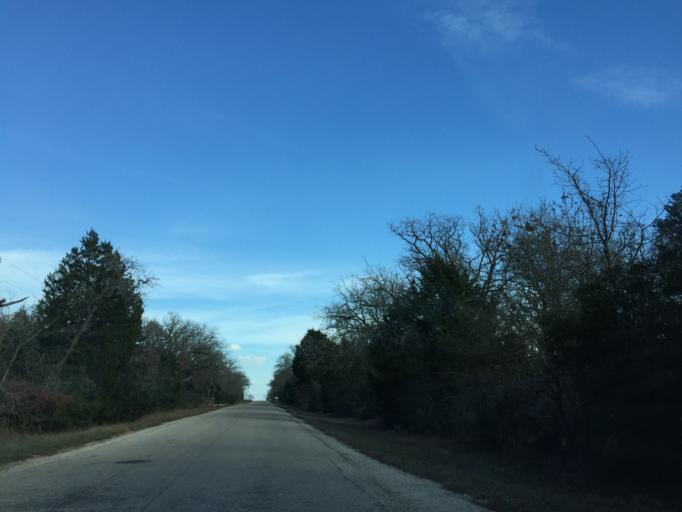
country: US
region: Texas
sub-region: Milam County
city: Thorndale
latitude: 30.4488
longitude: -97.2020
